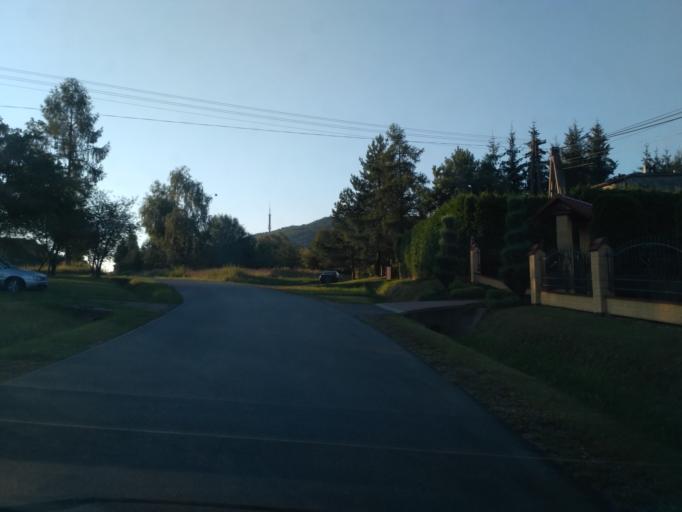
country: PL
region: Subcarpathian Voivodeship
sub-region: Powiat krosnienski
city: Korczyna
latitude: 49.7671
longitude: 21.7903
